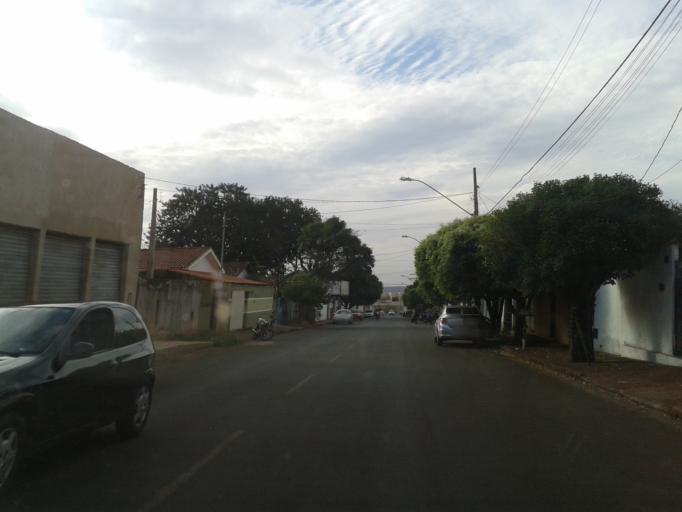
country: BR
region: Minas Gerais
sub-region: Ituiutaba
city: Ituiutaba
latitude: -18.9859
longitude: -49.4504
